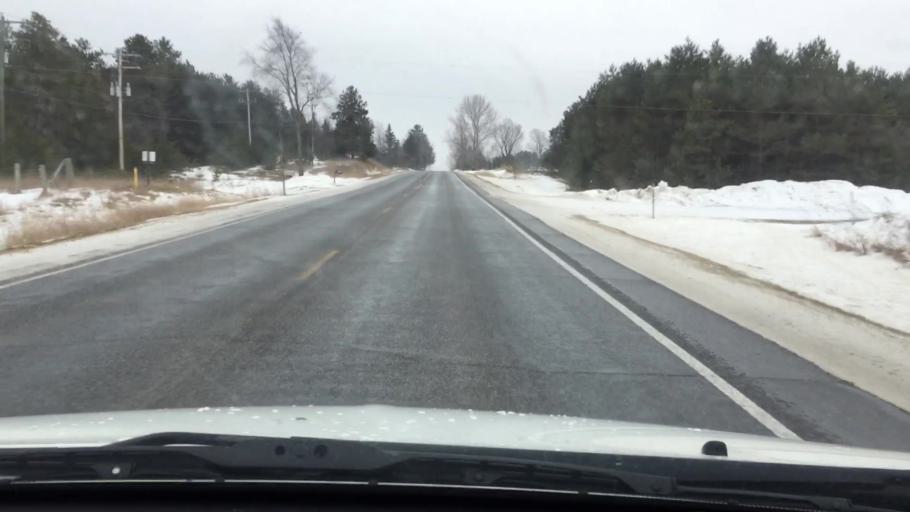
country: US
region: Michigan
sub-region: Wexford County
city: Cadillac
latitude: 44.0714
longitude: -85.4440
